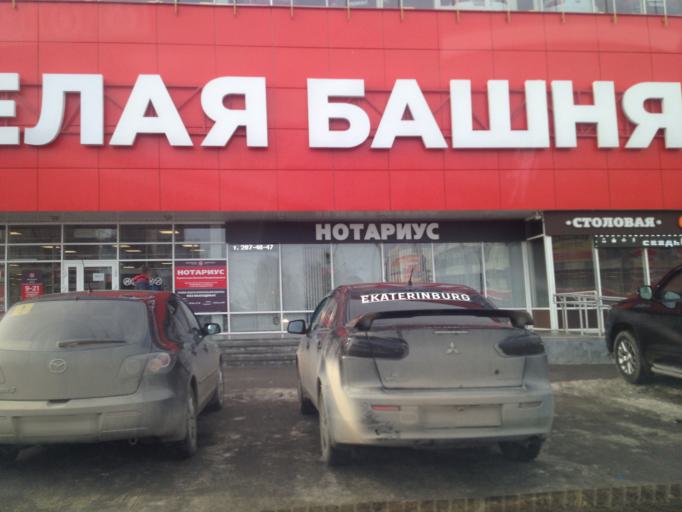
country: RU
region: Sverdlovsk
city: Yekaterinburg
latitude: 56.8925
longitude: 60.5710
